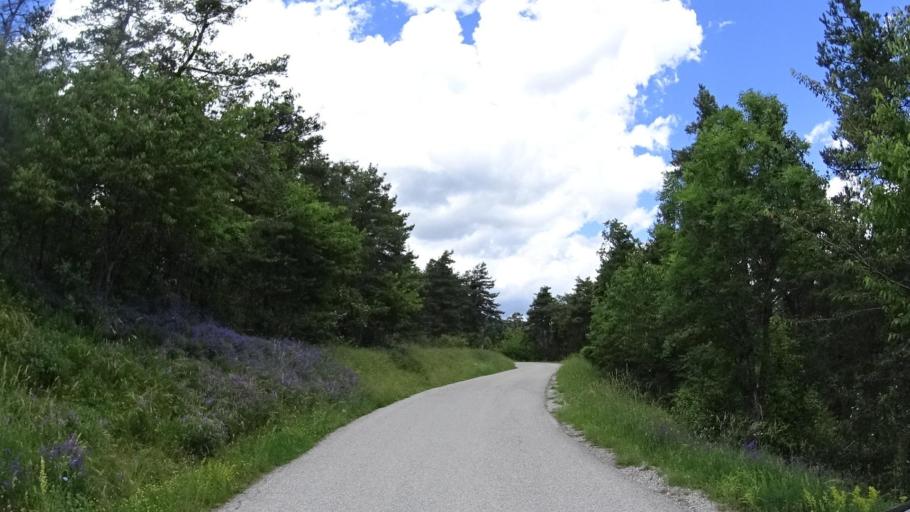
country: FR
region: Provence-Alpes-Cote d'Azur
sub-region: Departement des Alpes-de-Haute-Provence
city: Annot
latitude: 44.0139
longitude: 6.6283
